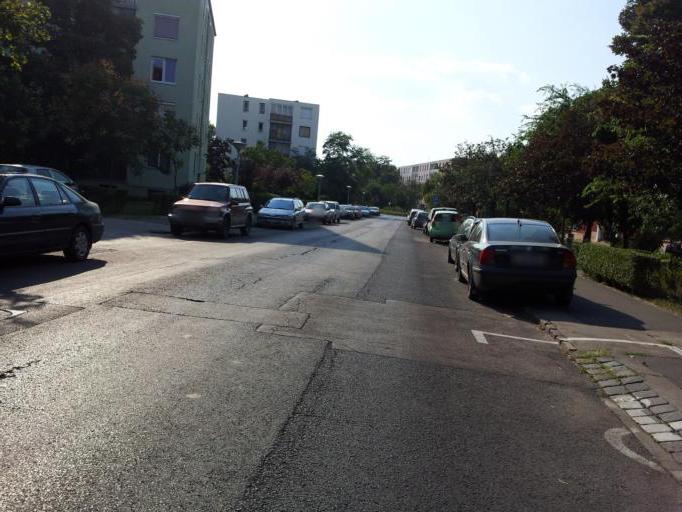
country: HU
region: Budapest
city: Budapest XX. keruelet
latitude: 47.4599
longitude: 19.1165
